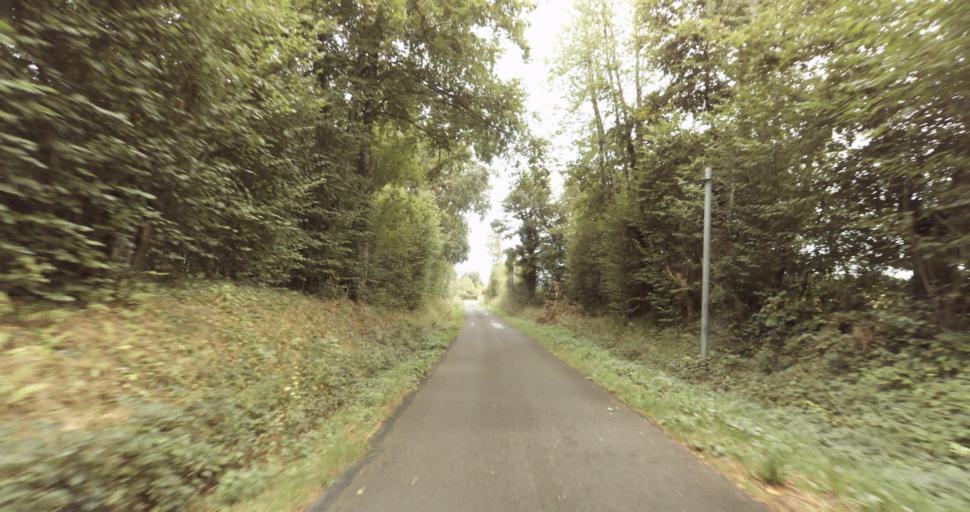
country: FR
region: Lower Normandy
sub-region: Departement de l'Orne
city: Gace
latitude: 48.7260
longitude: 0.2865
